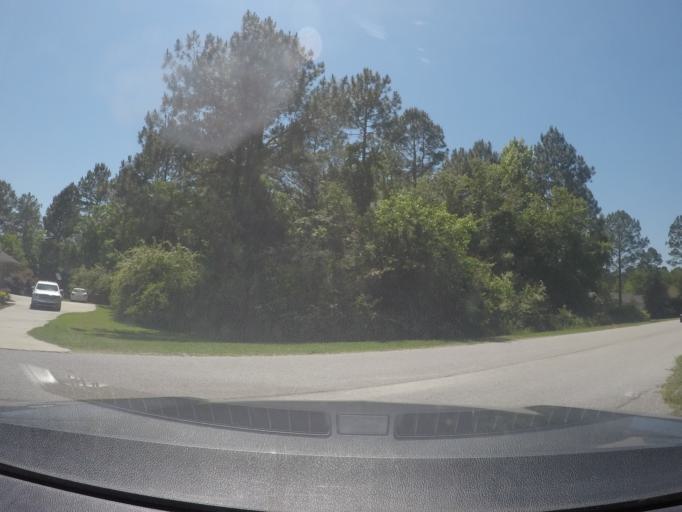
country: US
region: Georgia
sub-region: Bulloch County
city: Statesboro
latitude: 32.3511
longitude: -81.7607
